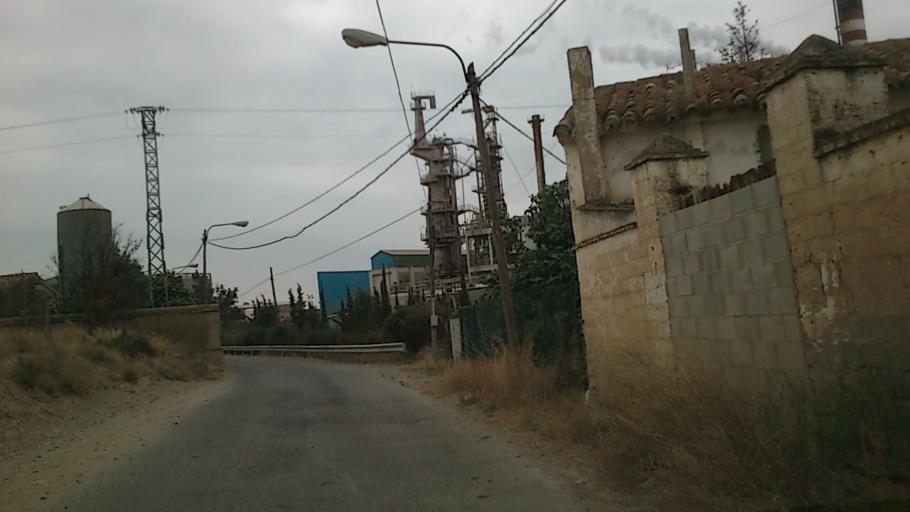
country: ES
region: Aragon
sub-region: Provincia de Zaragoza
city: Zaragoza
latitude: 41.6954
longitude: -0.8246
